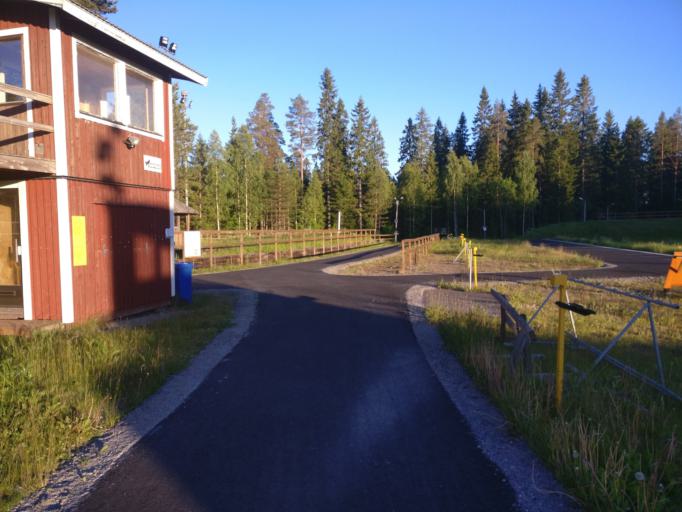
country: SE
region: Vaesternorrland
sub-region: Timra Kommun
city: Timra
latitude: 62.4613
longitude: 17.2939
